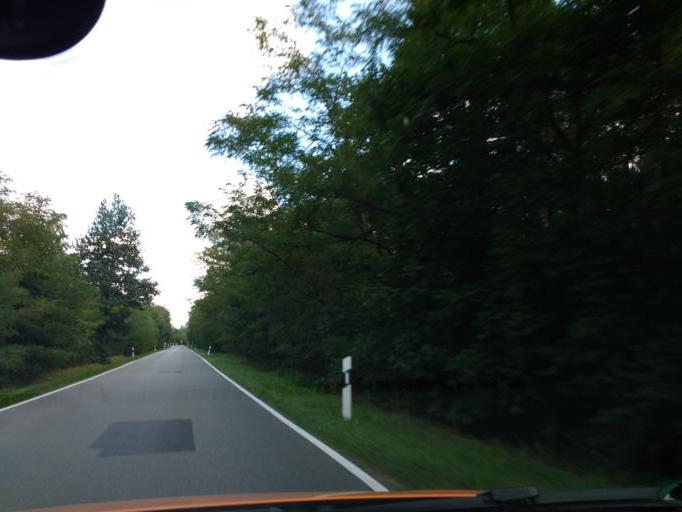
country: DE
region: Brandenburg
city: Wandlitz
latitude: 52.7351
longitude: 13.3936
